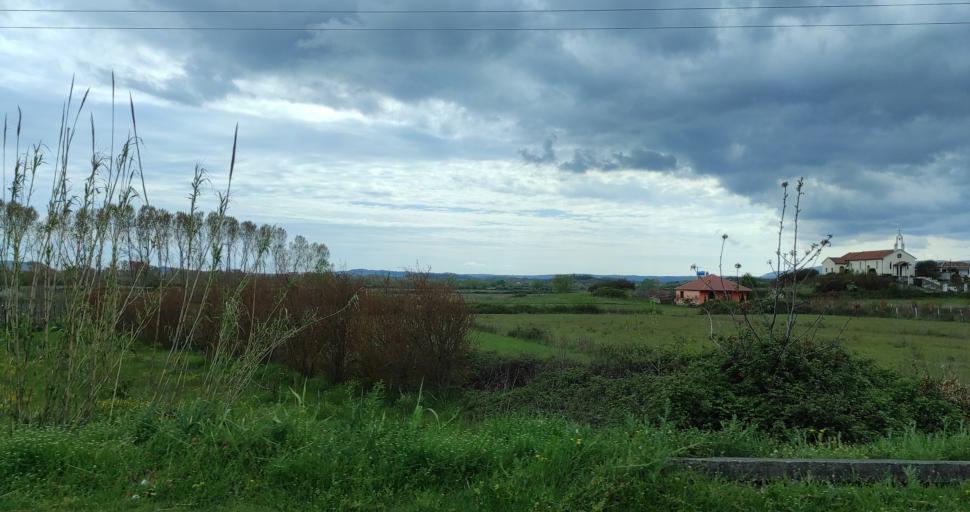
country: AL
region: Shkoder
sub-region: Rrethi i Shkodres
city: Dajc
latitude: 42.0154
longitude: 19.4004
